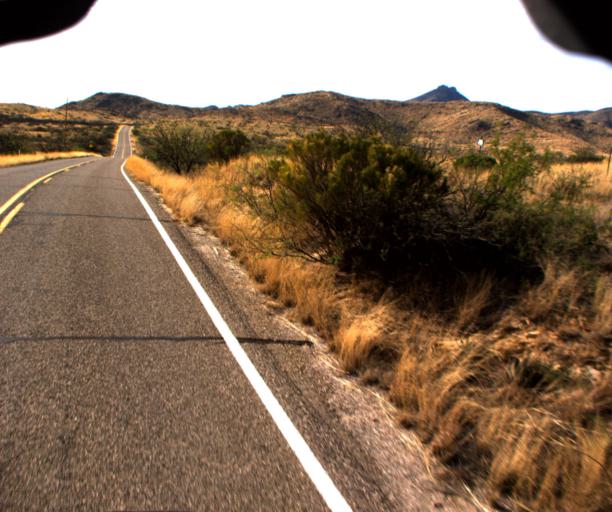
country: US
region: Arizona
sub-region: Cochise County
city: Willcox
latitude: 32.1605
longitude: -109.5702
